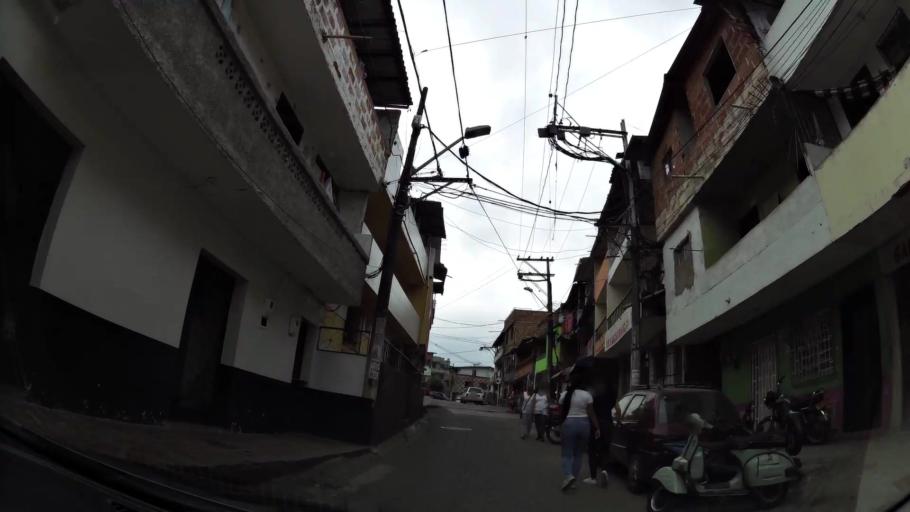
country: CO
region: Antioquia
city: Bello
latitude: 6.2956
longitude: -75.5526
